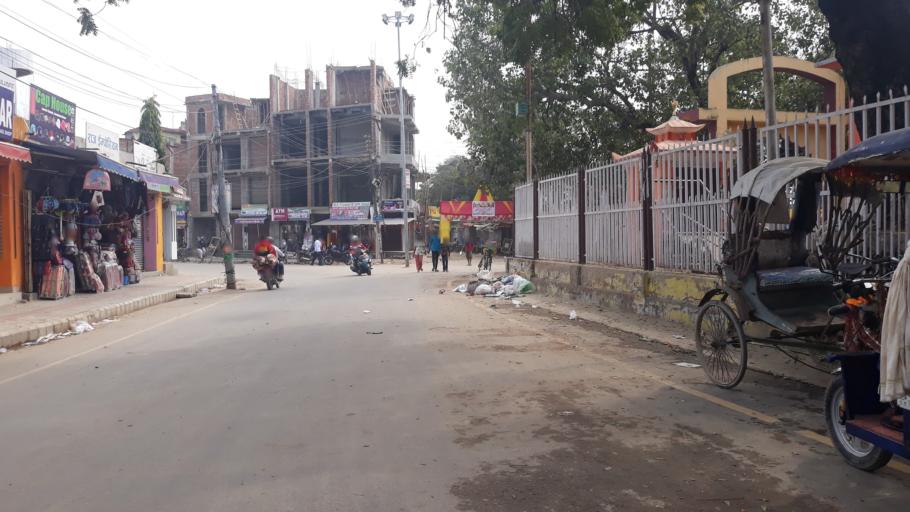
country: NP
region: Central Region
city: Janakpur
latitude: 26.7293
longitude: 85.9281
